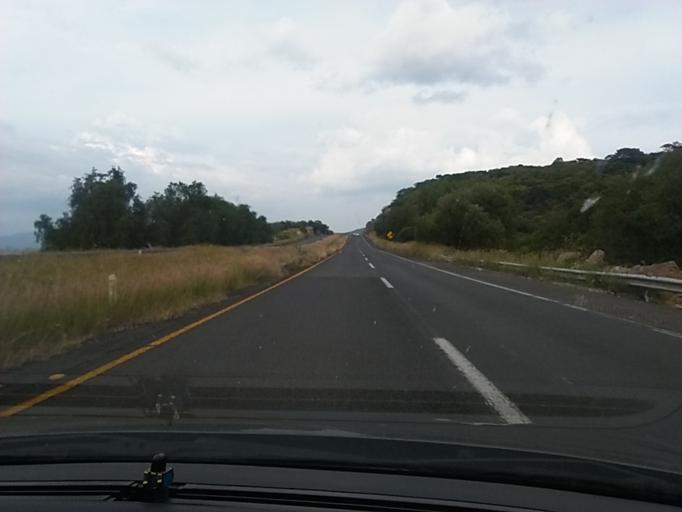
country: MX
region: Mexico
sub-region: Chapultepec
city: Chucandiro
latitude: 19.8842
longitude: -101.3376
